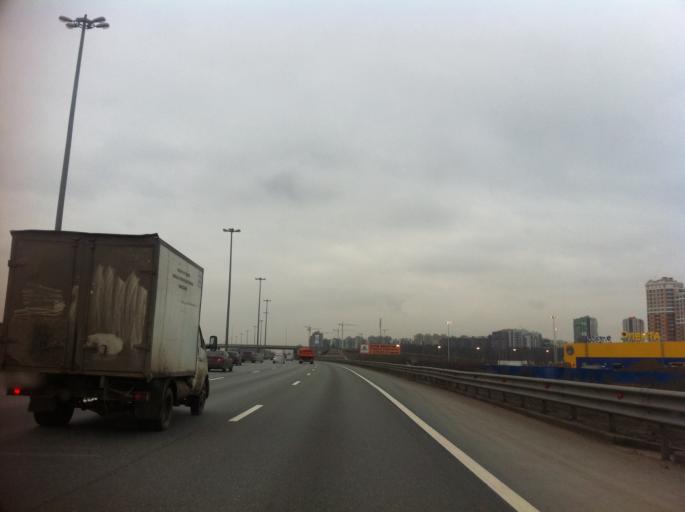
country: RU
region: St.-Petersburg
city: Krasnogvargeisky
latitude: 59.9195
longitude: 30.5260
